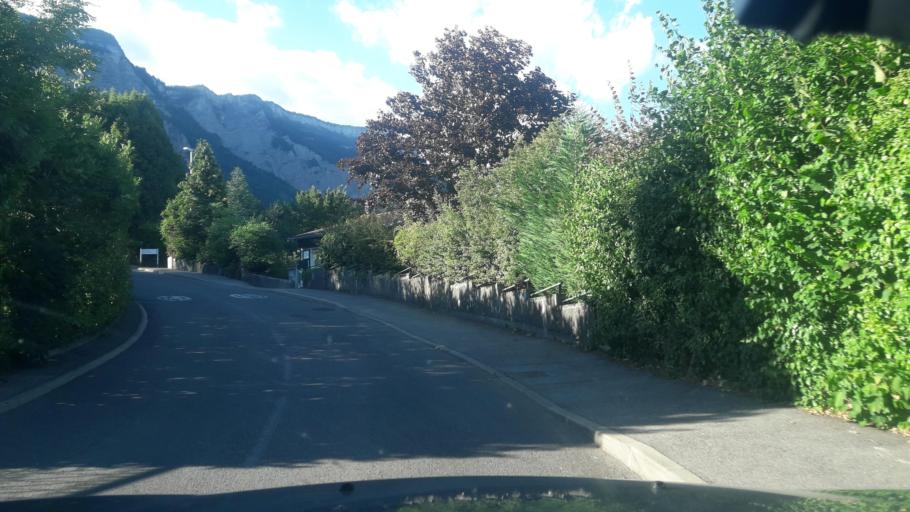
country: FR
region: Rhone-Alpes
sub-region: Departement de l'Isere
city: Biviers
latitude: 45.2368
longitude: 5.8055
